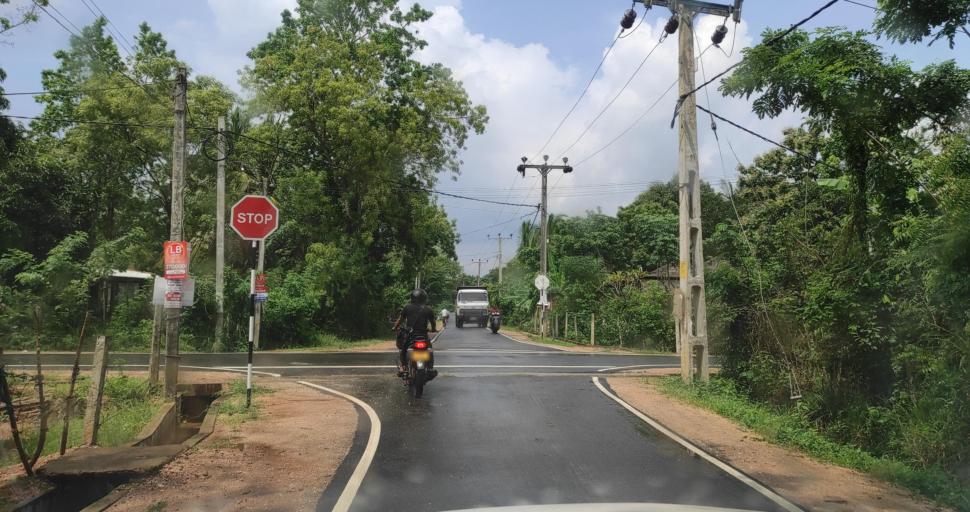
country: LK
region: Eastern Province
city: Trincomalee
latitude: 8.3722
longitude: 81.0118
